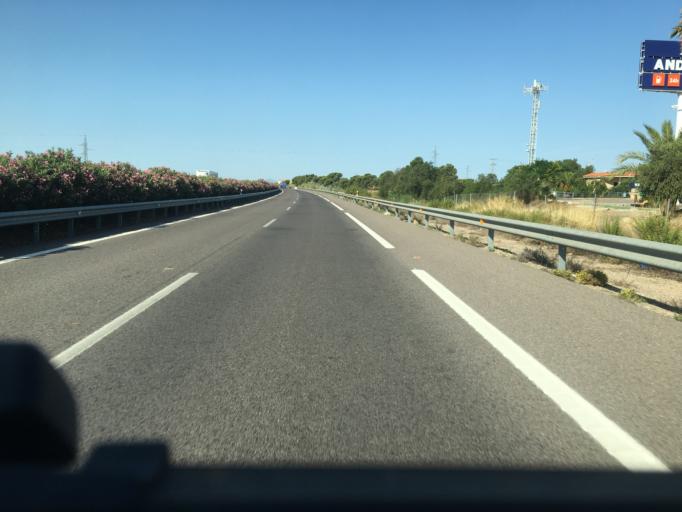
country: ES
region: Murcia
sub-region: Murcia
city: Puerto Lumbreras
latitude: 37.4812
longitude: -1.8688
